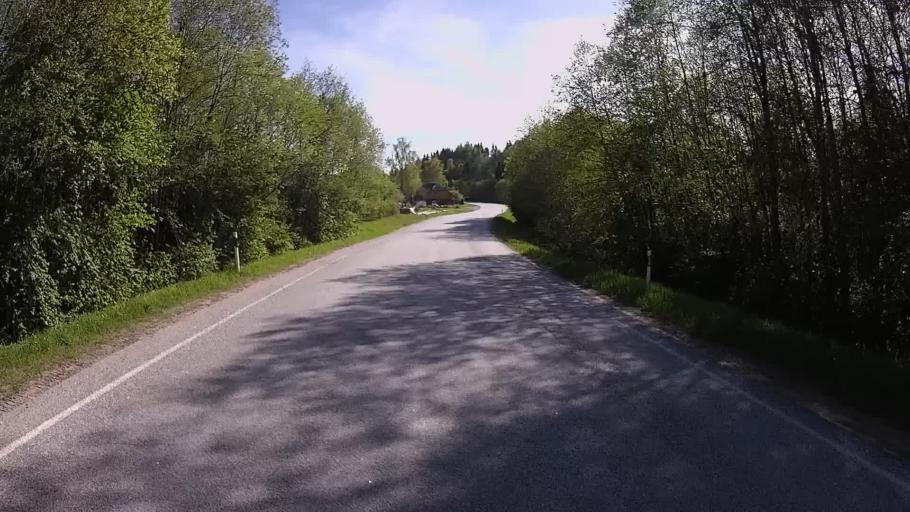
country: EE
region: Vorumaa
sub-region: Antsla vald
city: Vana-Antsla
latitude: 58.0211
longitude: 26.5028
